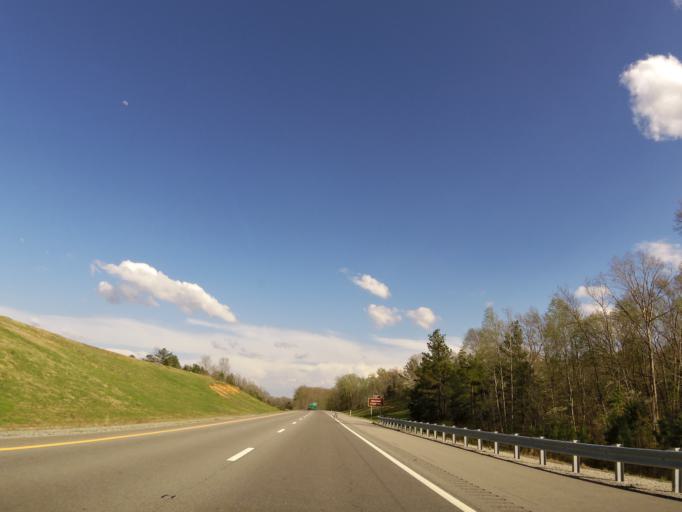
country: US
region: Tennessee
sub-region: Williamson County
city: Fairview
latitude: 35.8918
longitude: -87.1253
